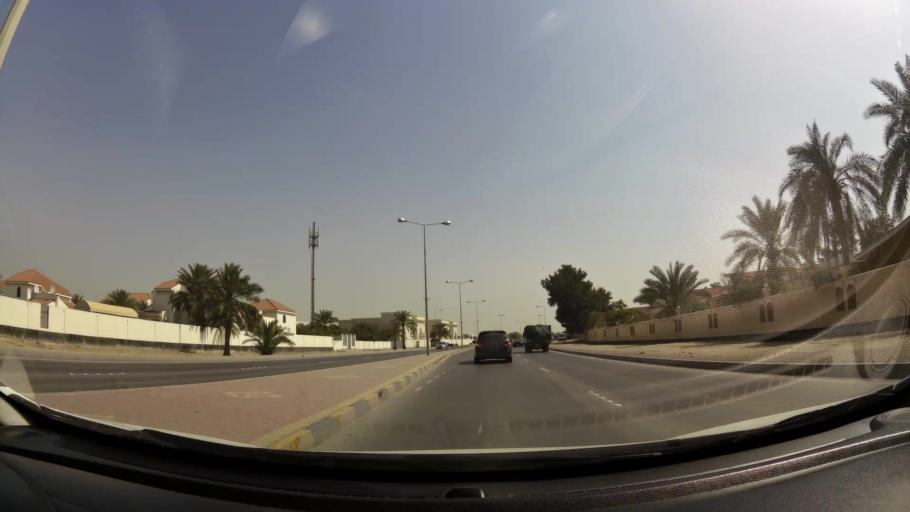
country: BH
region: Northern
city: Madinat `Isa
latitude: 26.1926
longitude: 50.4643
